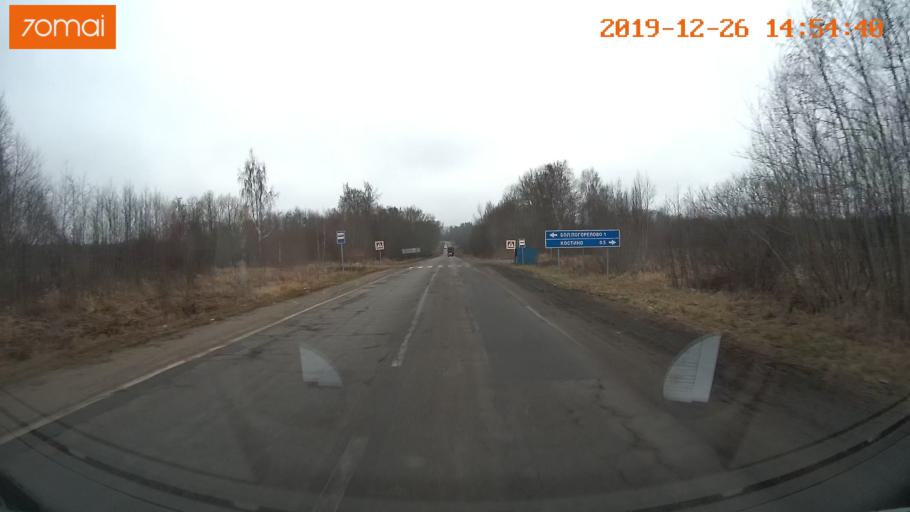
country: RU
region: Jaroslavl
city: Rybinsk
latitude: 58.3060
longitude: 38.8824
